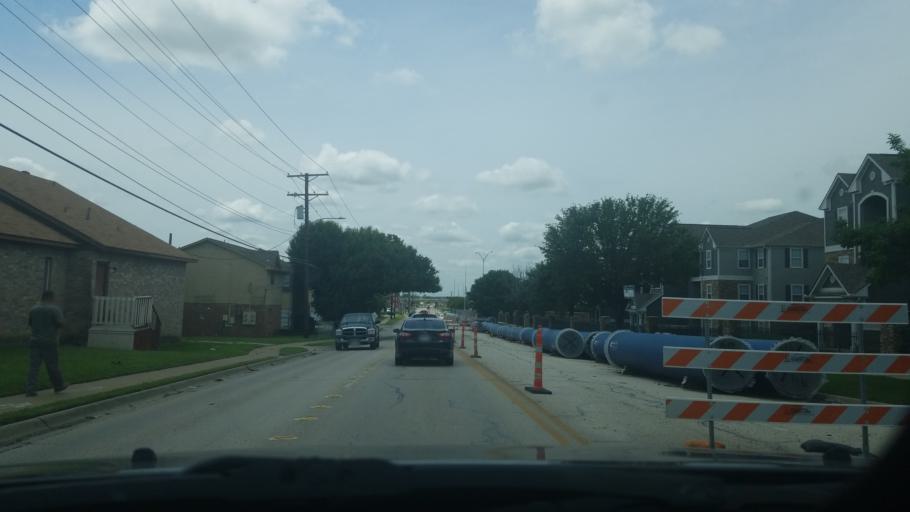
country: US
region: Texas
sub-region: Denton County
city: Denton
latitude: 33.2138
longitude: -97.1614
